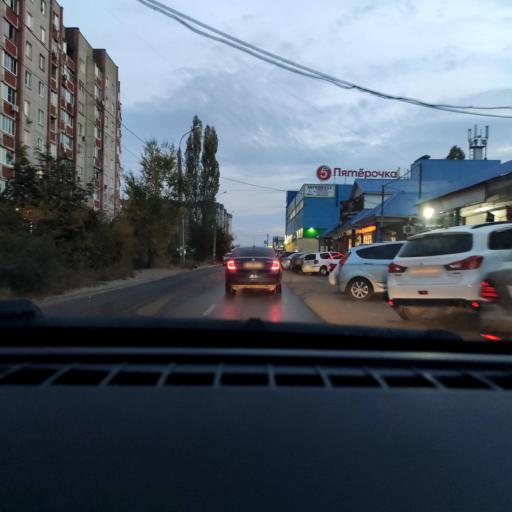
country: RU
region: Voronezj
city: Somovo
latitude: 51.7376
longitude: 39.2913
